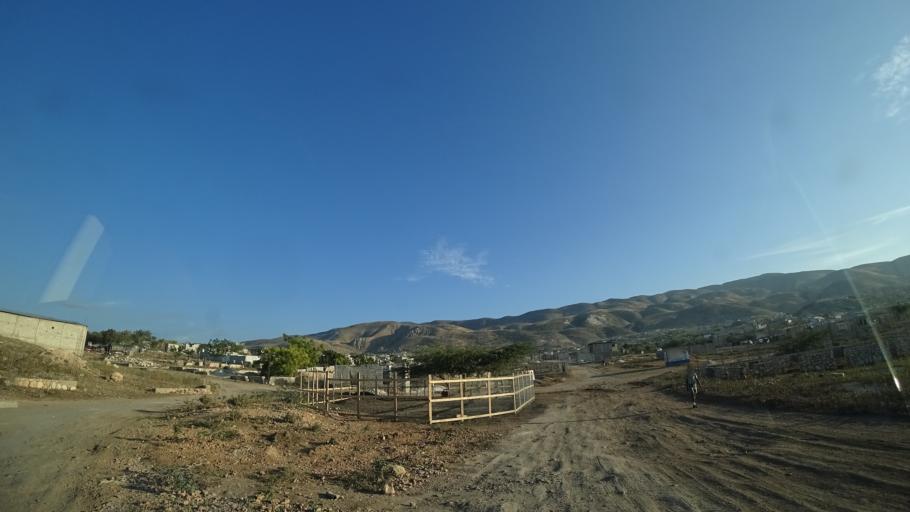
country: HT
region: Ouest
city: Cabaret
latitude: 18.6850
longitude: -72.3186
